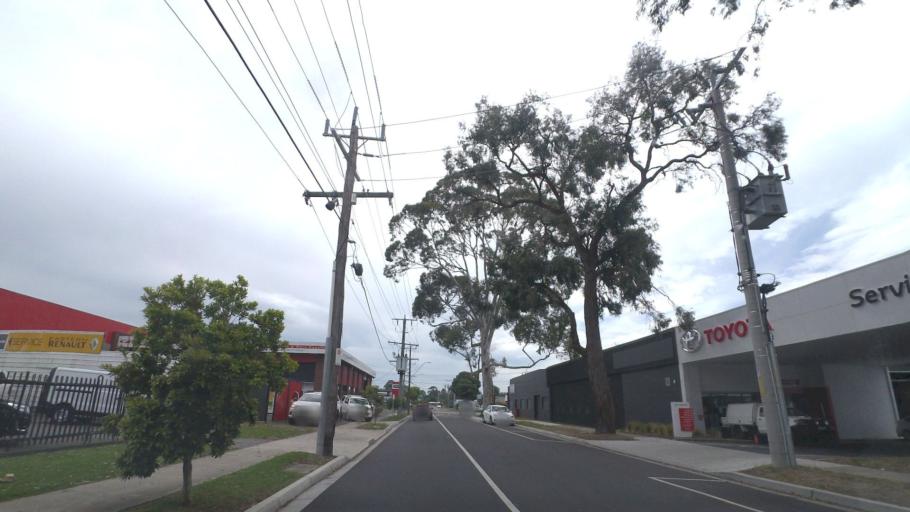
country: AU
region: Victoria
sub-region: Maroondah
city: Croydon North
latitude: -37.7962
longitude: 145.2852
